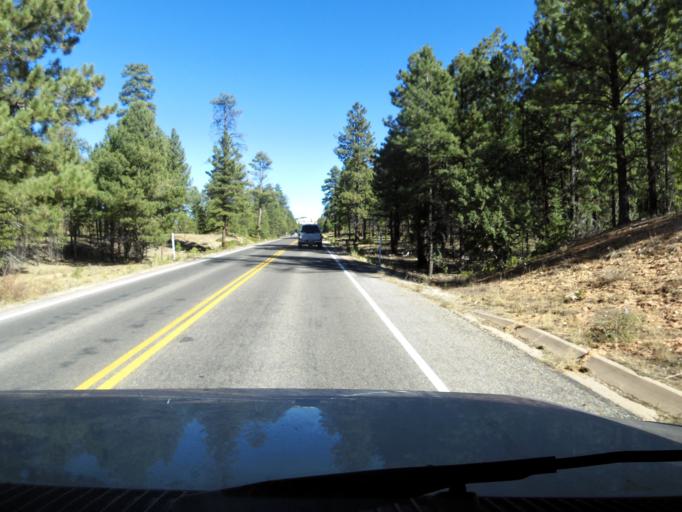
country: US
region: Utah
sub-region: Garfield County
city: Panguitch
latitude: 37.6058
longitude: -112.2034
